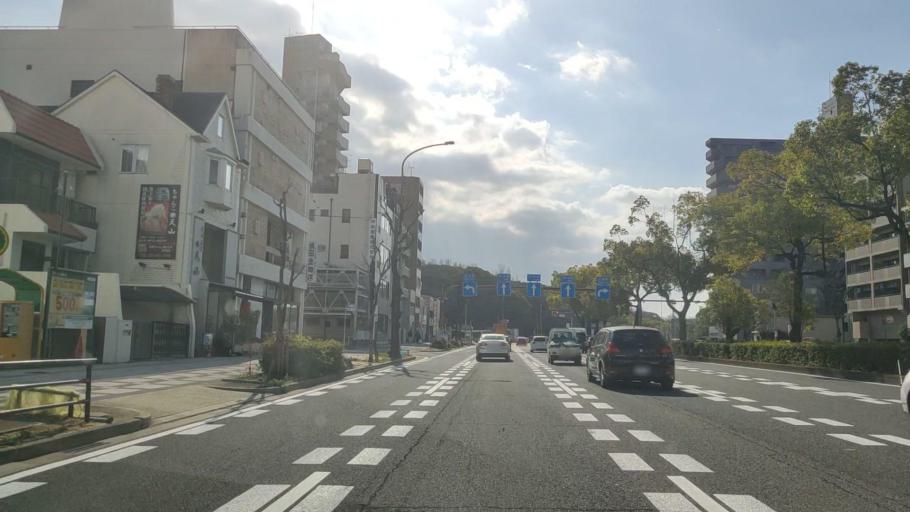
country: JP
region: Aichi
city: Nagoya-shi
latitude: 35.1293
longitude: 136.9059
